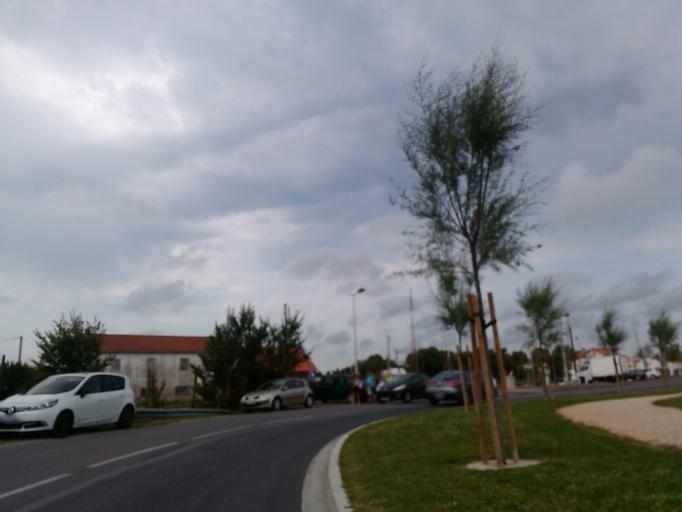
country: FR
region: Poitou-Charentes
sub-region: Departement de la Charente-Maritime
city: La Tremblade
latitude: 45.7677
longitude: -1.1359
